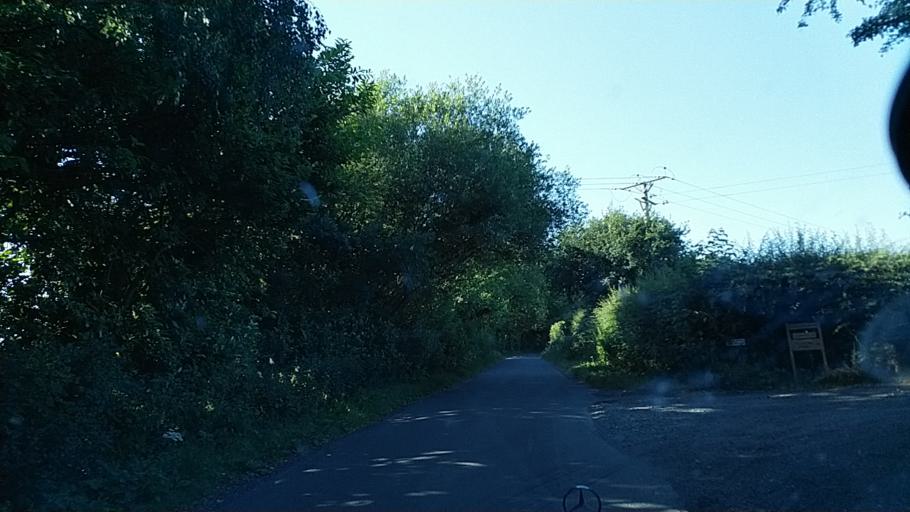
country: GB
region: England
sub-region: Warwickshire
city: Wroxall
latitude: 52.3064
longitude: -1.6377
